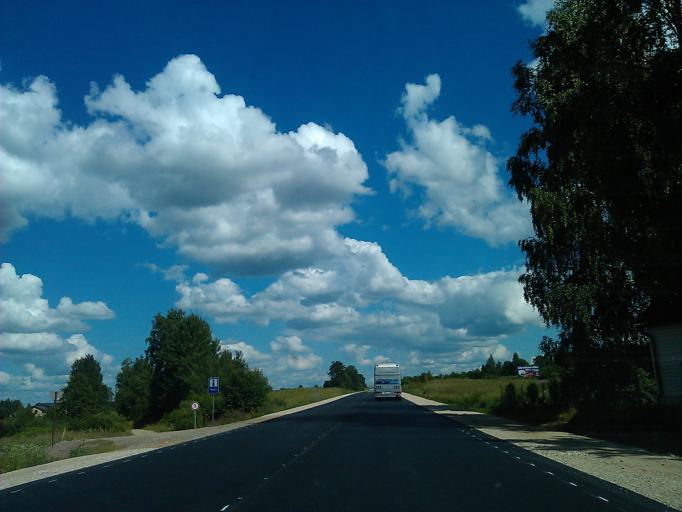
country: LV
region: Rezekne
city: Rezekne
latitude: 56.5330
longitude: 27.2509
